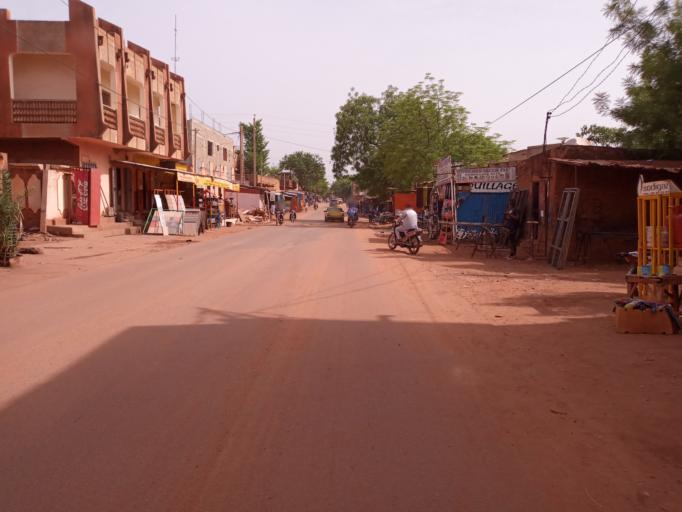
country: ML
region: Bamako
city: Bamako
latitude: 12.6079
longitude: -7.9521
